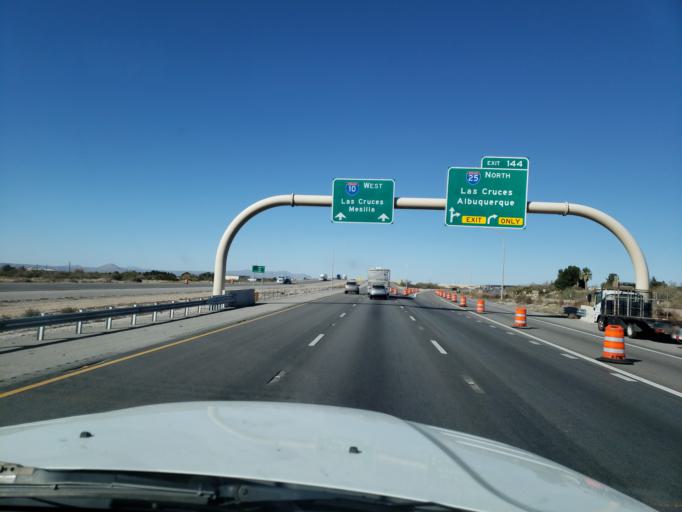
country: US
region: New Mexico
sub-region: Dona Ana County
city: University Park
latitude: 32.2542
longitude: -106.7273
